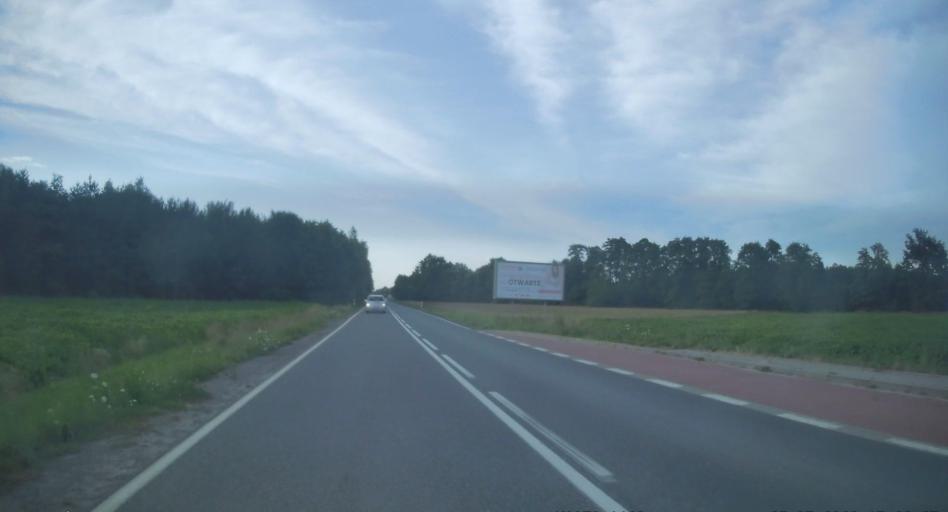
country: PL
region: Lesser Poland Voivodeship
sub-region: Powiat brzeski
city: Szczurowa
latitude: 50.0782
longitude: 20.6335
